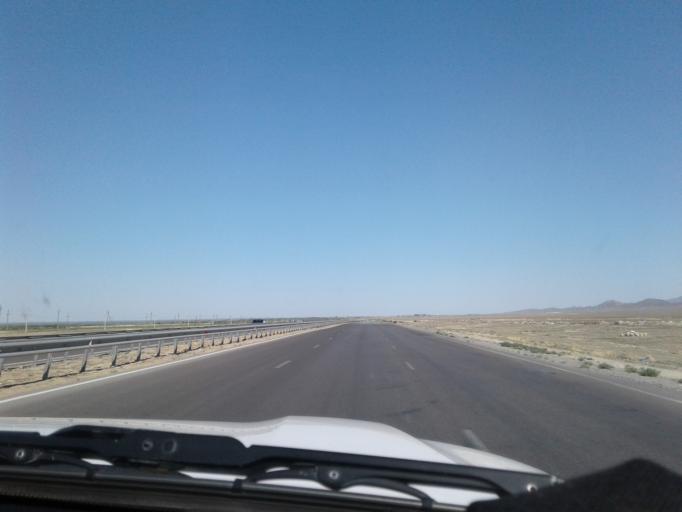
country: IR
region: Razavi Khorasan
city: Dargaz
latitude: 37.7519
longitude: 58.9472
